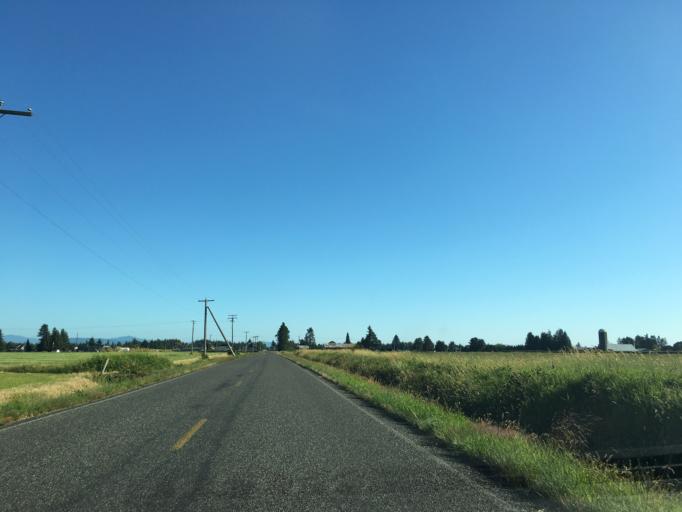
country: US
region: Washington
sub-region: Whatcom County
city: Lynden
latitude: 48.9700
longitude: -122.4520
